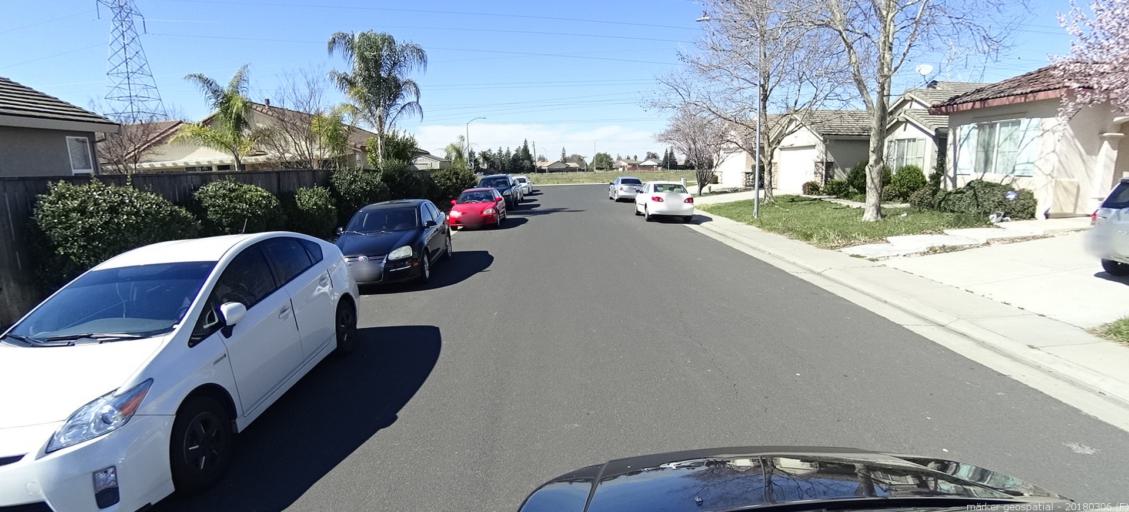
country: US
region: California
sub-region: Sacramento County
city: Vineyard
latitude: 38.4560
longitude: -121.3504
